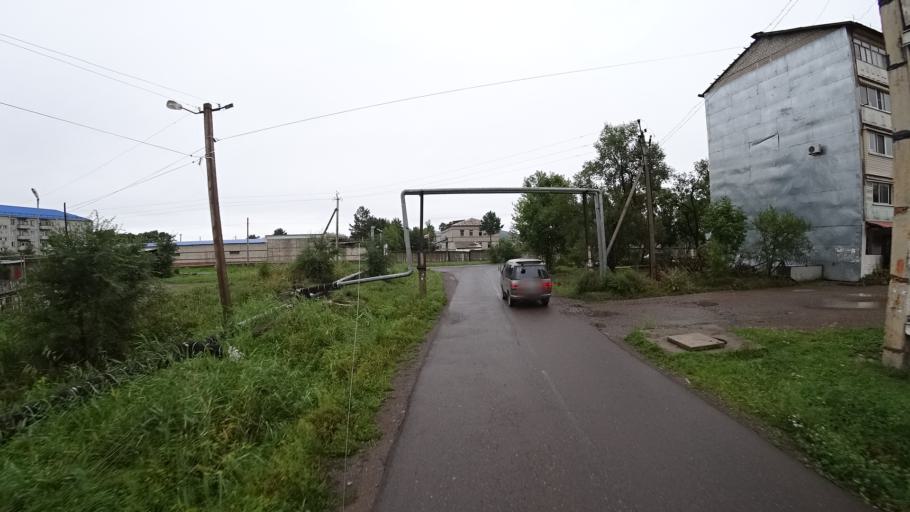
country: RU
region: Primorskiy
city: Monastyrishche
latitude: 44.2076
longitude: 132.4480
